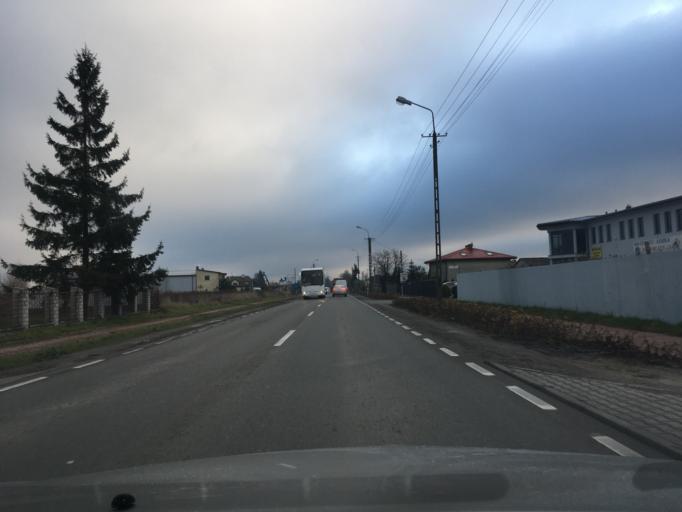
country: PL
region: Masovian Voivodeship
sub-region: Powiat piaseczynski
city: Lesznowola
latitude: 52.0852
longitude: 20.9519
